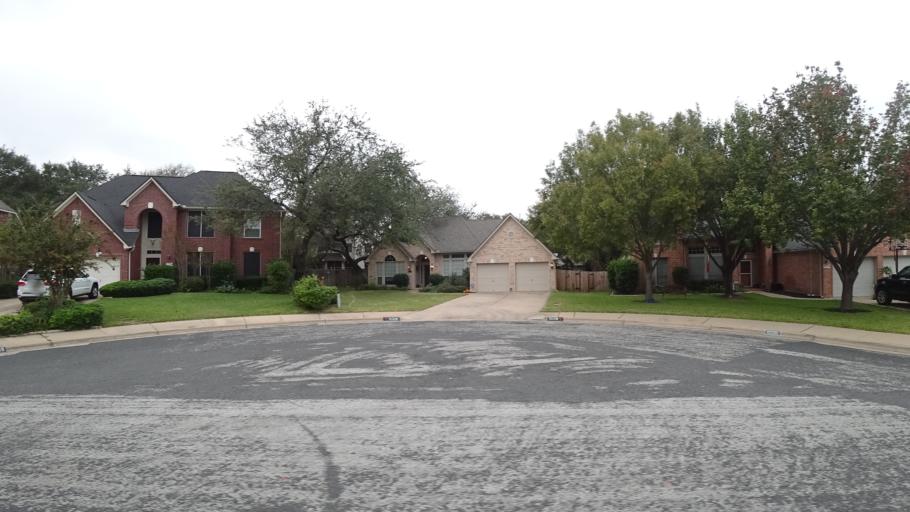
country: US
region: Texas
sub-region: Williamson County
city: Anderson Mill
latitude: 30.4349
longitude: -97.8209
